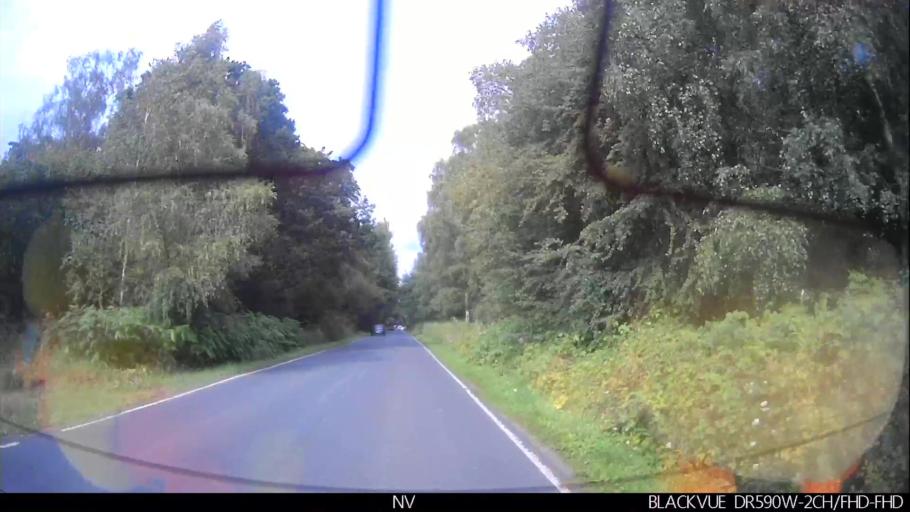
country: GB
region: England
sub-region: North Yorkshire
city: Strensall
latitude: 54.0353
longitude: -1.0256
